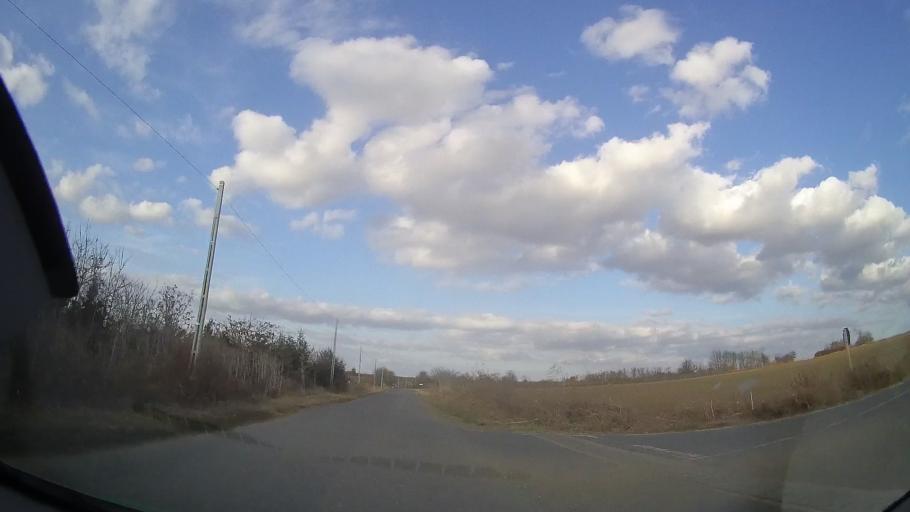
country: RO
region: Constanta
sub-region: Comuna Cerchezu
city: Cerchezu
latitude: 43.8514
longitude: 28.1006
